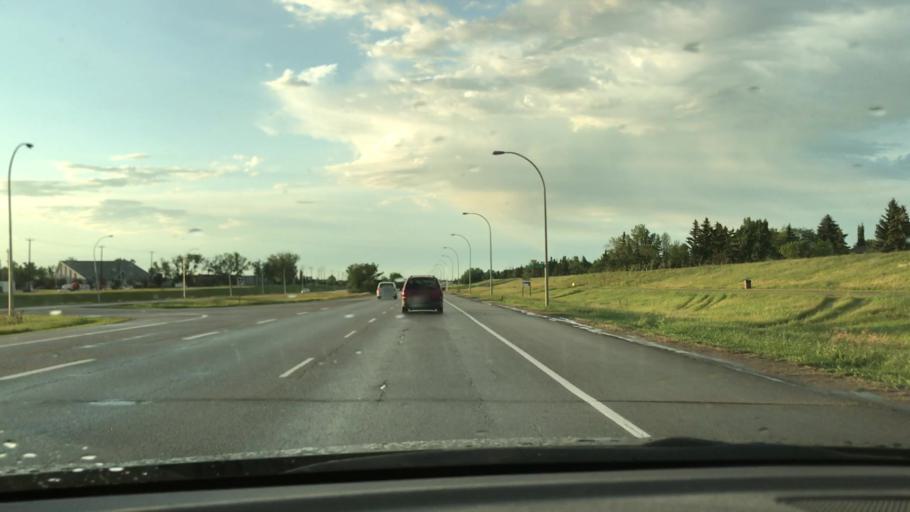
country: CA
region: Alberta
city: Edmonton
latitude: 53.4681
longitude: -113.4663
